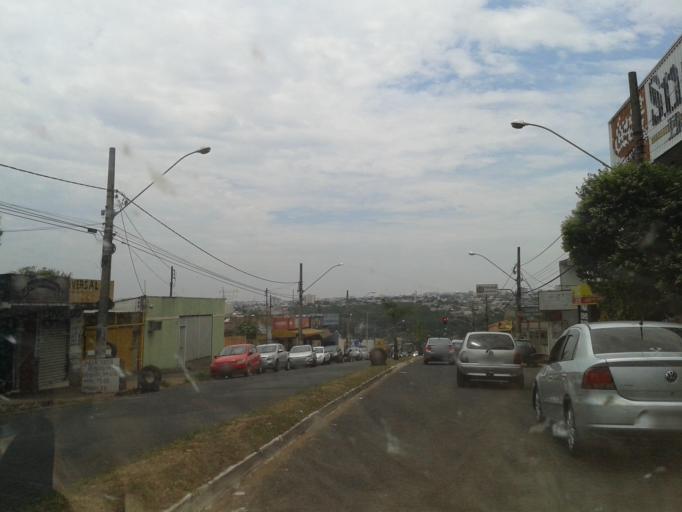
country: BR
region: Minas Gerais
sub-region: Uberlandia
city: Uberlandia
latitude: -18.9100
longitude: -48.3160
